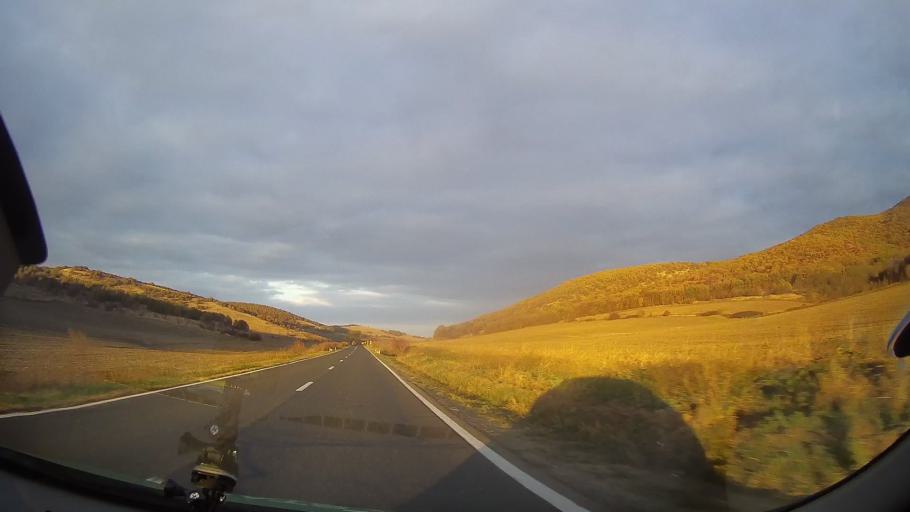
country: RO
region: Tulcea
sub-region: Comuna Ciucurova
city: Ciucurova
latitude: 44.9550
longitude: 28.5147
